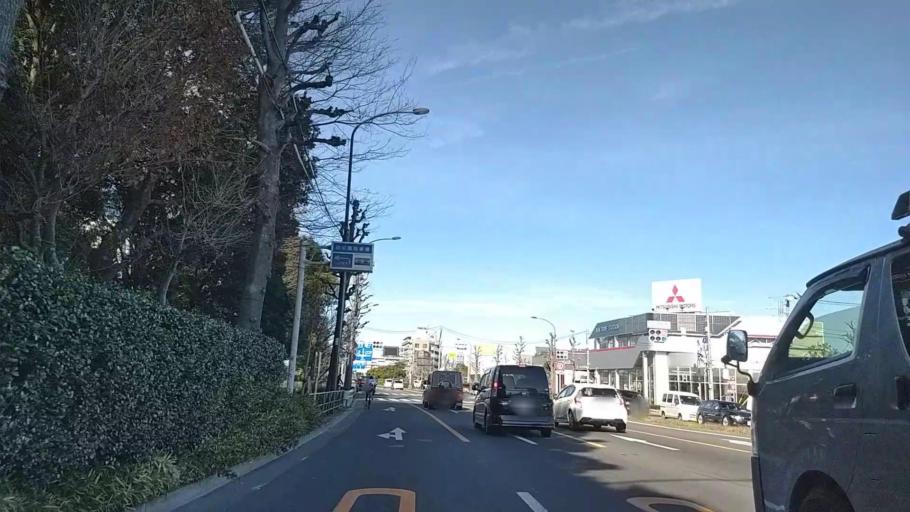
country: JP
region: Tokyo
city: Chofugaoka
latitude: 35.6321
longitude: 139.6247
